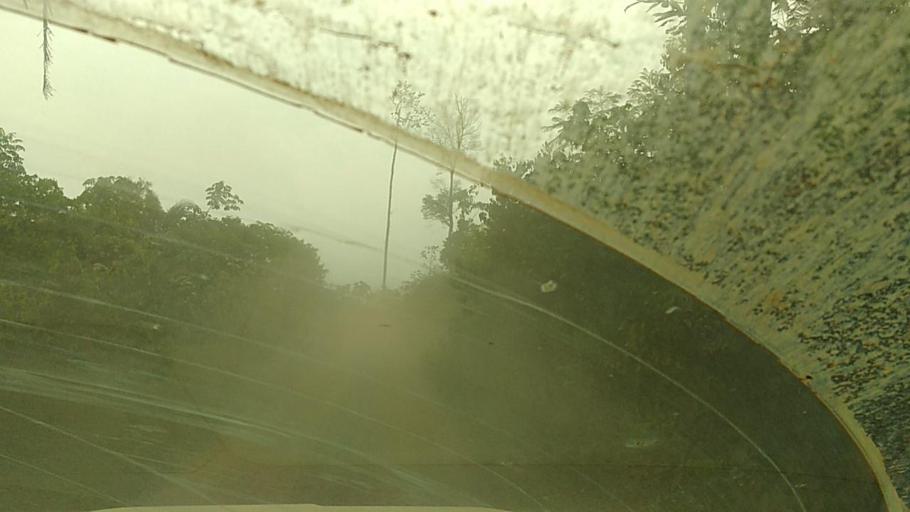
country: BR
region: Rondonia
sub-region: Porto Velho
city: Porto Velho
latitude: -8.7729
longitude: -63.1961
